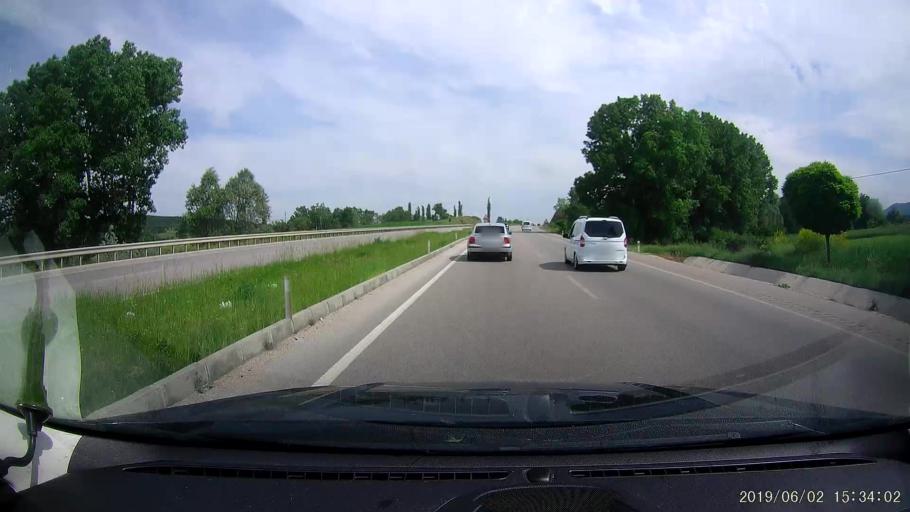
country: TR
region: Amasya
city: Saraycik
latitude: 40.9177
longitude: 35.1700
